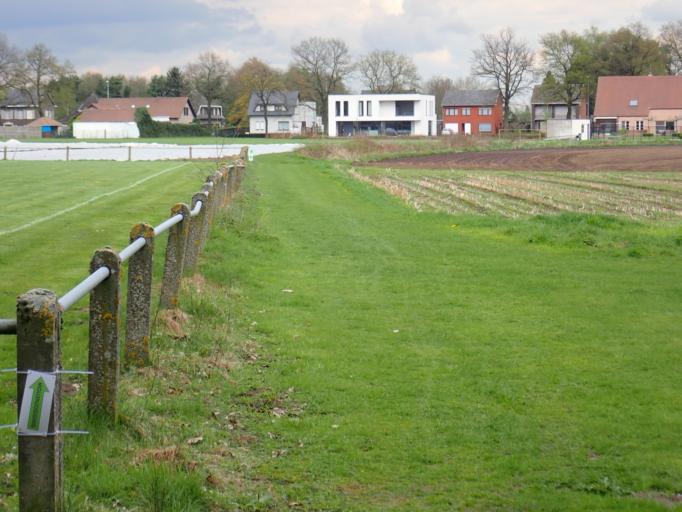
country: BE
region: Flanders
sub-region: Provincie Antwerpen
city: Lille
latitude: 51.2207
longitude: 4.8358
